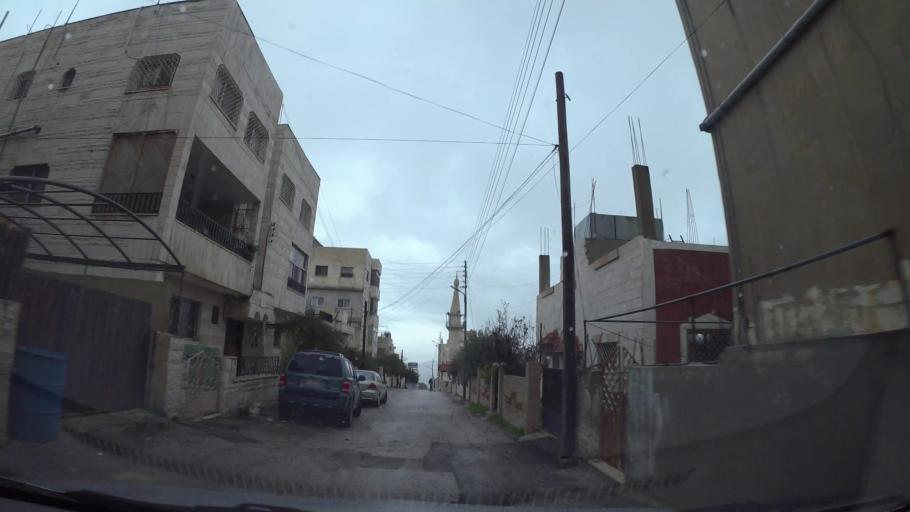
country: JO
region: Amman
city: Al Jubayhah
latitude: 32.0337
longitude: 35.8369
